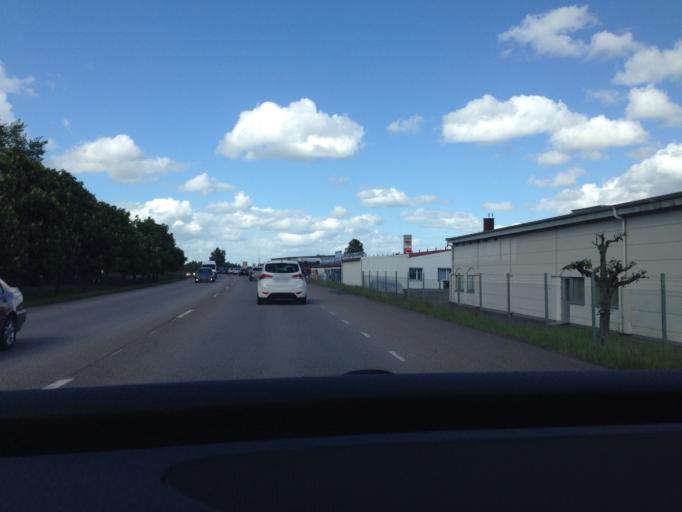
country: SE
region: Vaestra Goetaland
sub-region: Skovde Kommun
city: Skoevde
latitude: 58.4029
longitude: 13.8494
